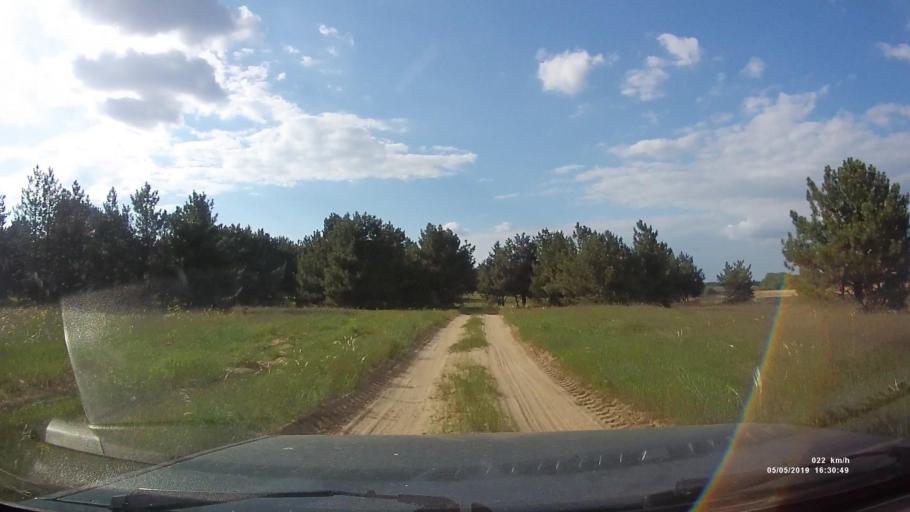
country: RU
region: Rostov
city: Ust'-Donetskiy
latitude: 47.7747
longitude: 41.0156
